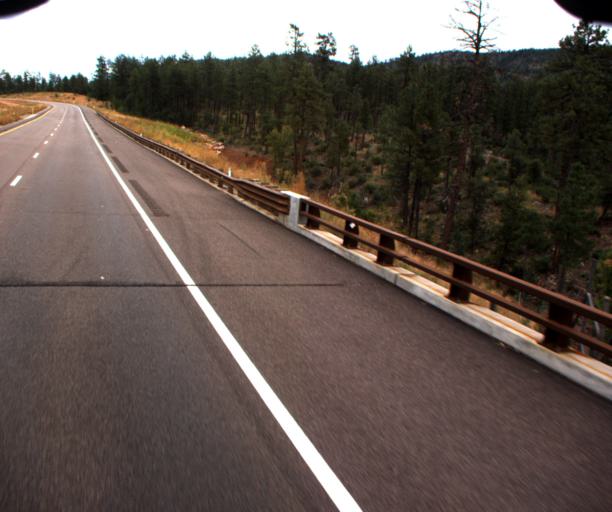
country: US
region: Arizona
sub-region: Gila County
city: Star Valley
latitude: 34.3115
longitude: -111.0483
